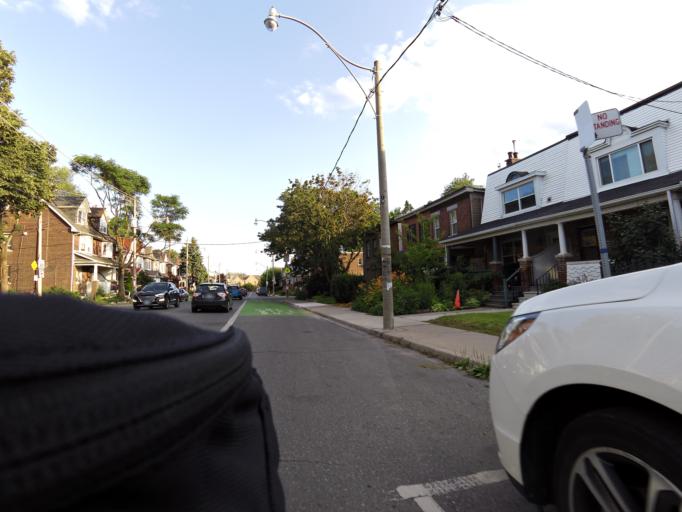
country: CA
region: Ontario
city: Toronto
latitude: 43.6665
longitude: -79.3262
